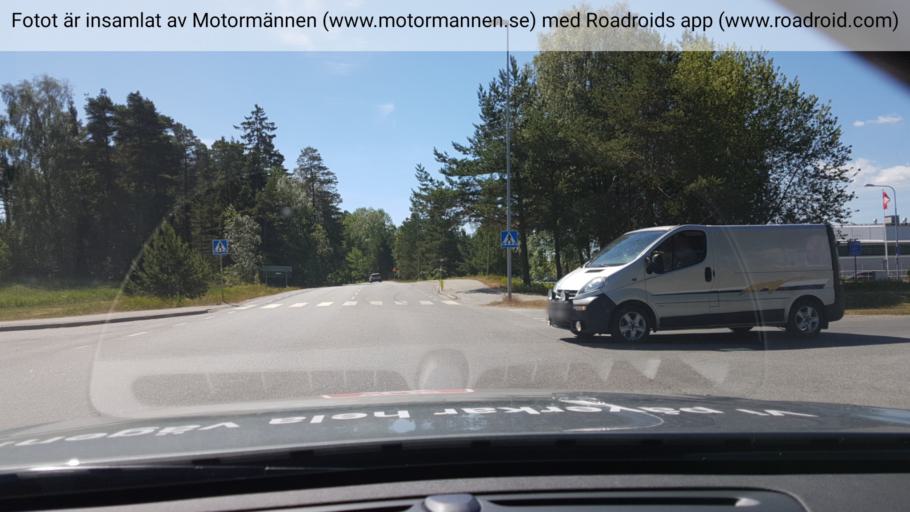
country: SE
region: Stockholm
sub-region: Haninge Kommun
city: Haninge
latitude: 59.1649
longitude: 18.1625
